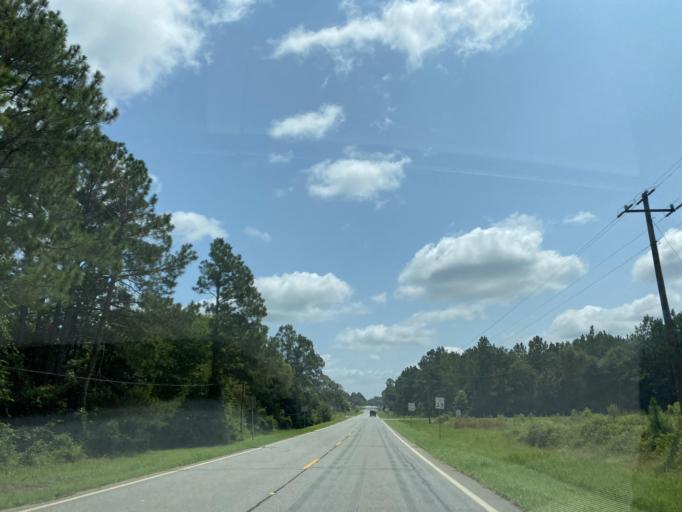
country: US
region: Georgia
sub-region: Telfair County
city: Helena
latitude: 32.0176
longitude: -83.0688
